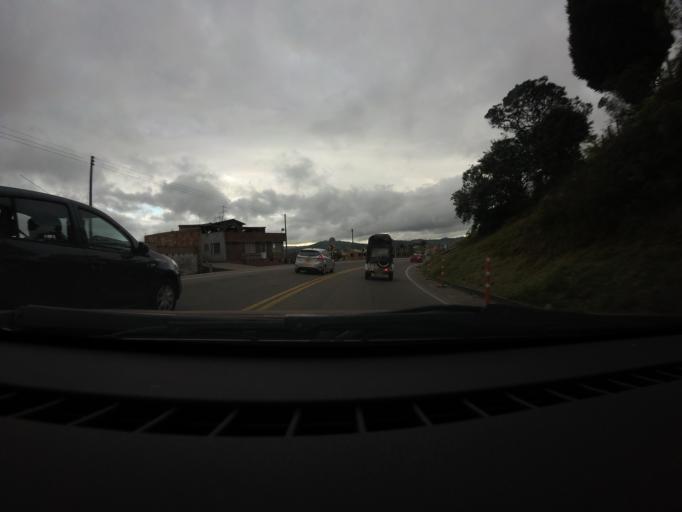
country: CO
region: Boyaca
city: Samaca
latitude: 5.4653
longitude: -73.4155
